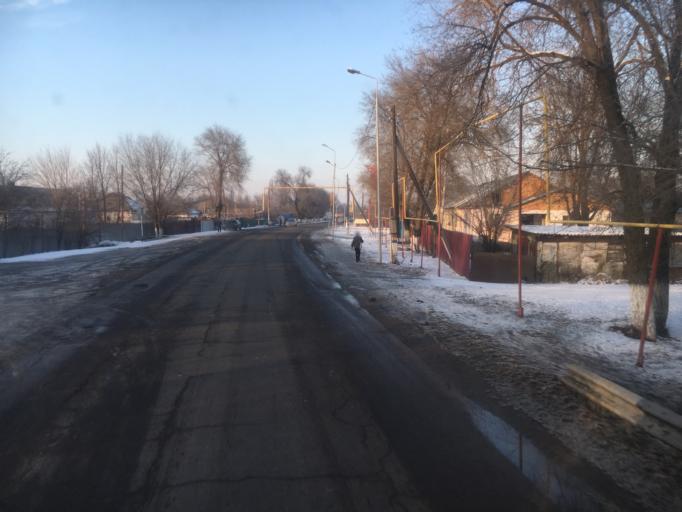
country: KZ
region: Almaty Oblysy
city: Burunday
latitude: 43.3665
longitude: 76.6414
